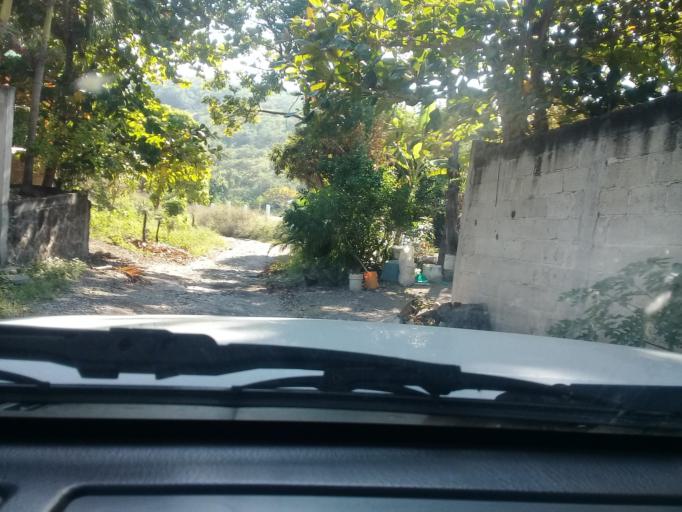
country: MX
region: Veracruz
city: Rinconada
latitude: 19.4011
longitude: -96.5570
